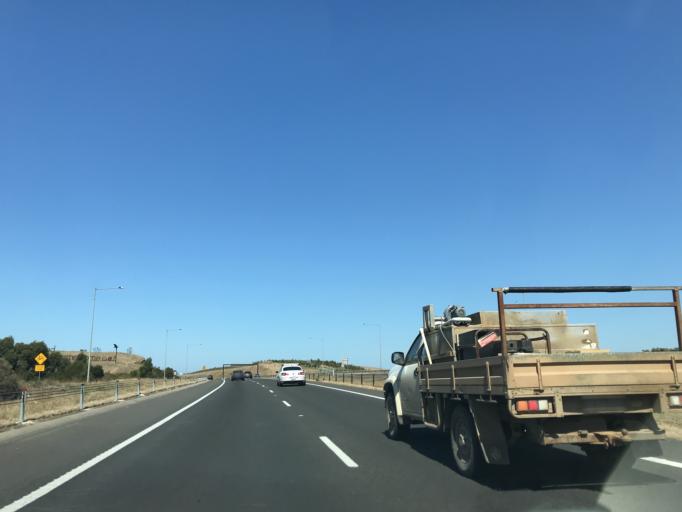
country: AU
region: Victoria
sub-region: Greater Geelong
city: Wandana Heights
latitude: -38.1732
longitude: 144.2928
